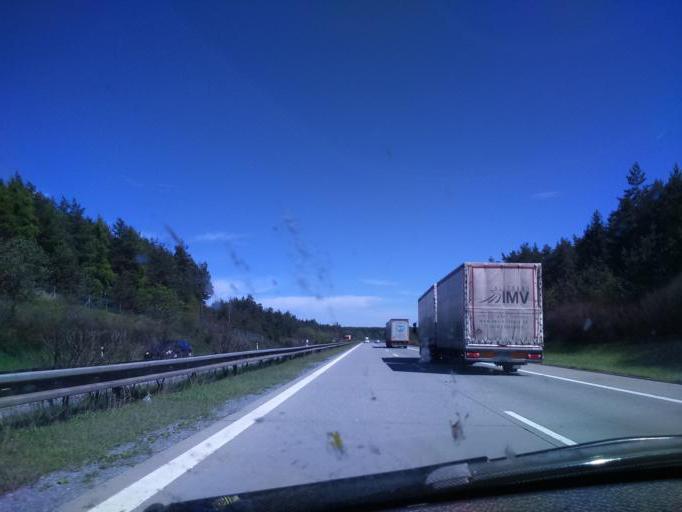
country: CZ
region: Plzensky
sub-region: Okres Tachov
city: Kladruby
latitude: 49.7193
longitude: 12.9084
